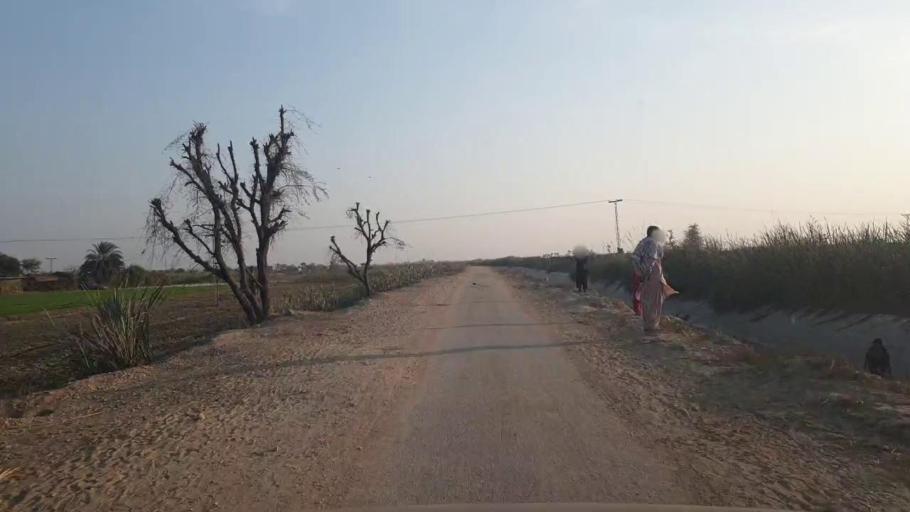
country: PK
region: Sindh
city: Bhit Shah
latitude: 25.8696
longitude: 68.5497
